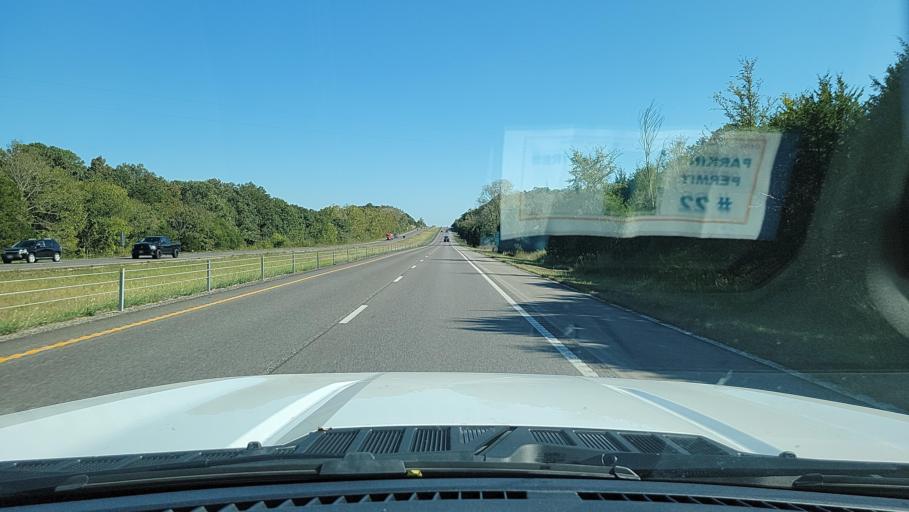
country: US
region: Missouri
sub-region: Sainte Genevieve County
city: Sainte Genevieve
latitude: 37.9617
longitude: -90.1699
